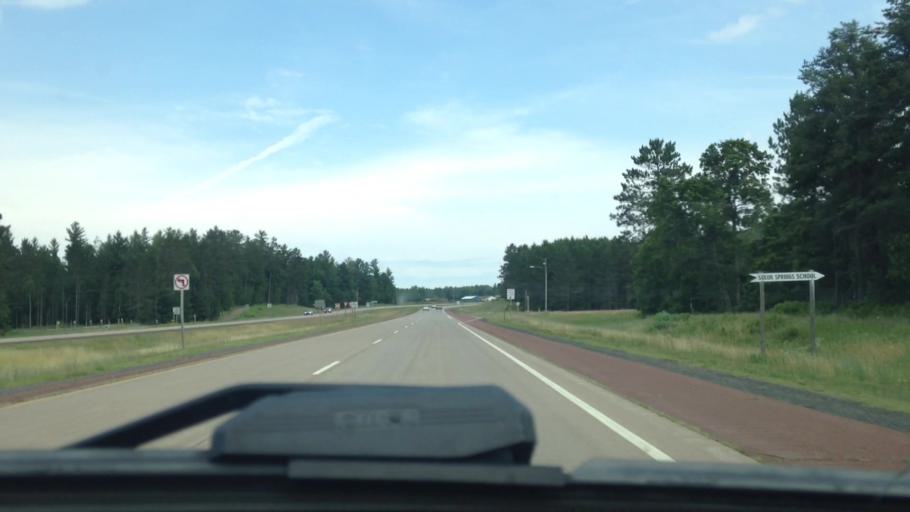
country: US
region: Wisconsin
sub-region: Douglas County
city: Lake Nebagamon
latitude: 46.3440
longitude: -91.8342
